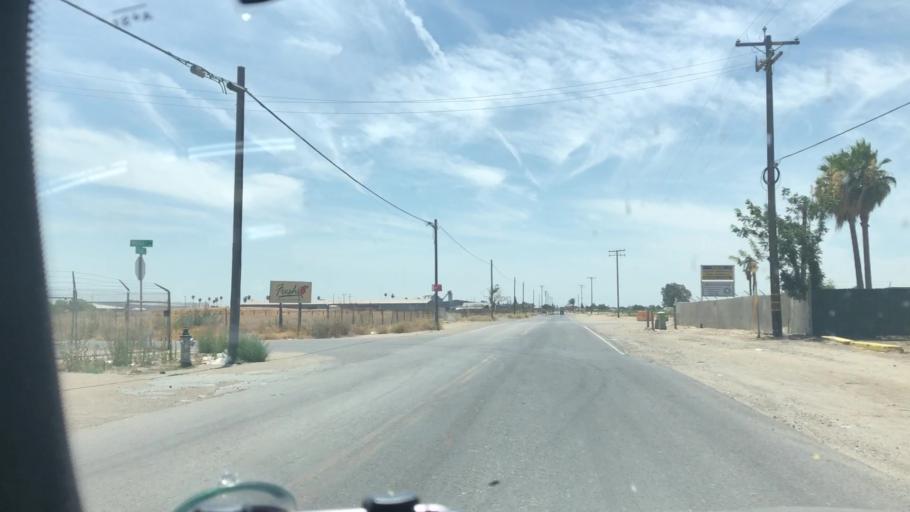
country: US
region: California
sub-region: Fresno County
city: Easton
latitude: 36.6853
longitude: -119.7547
